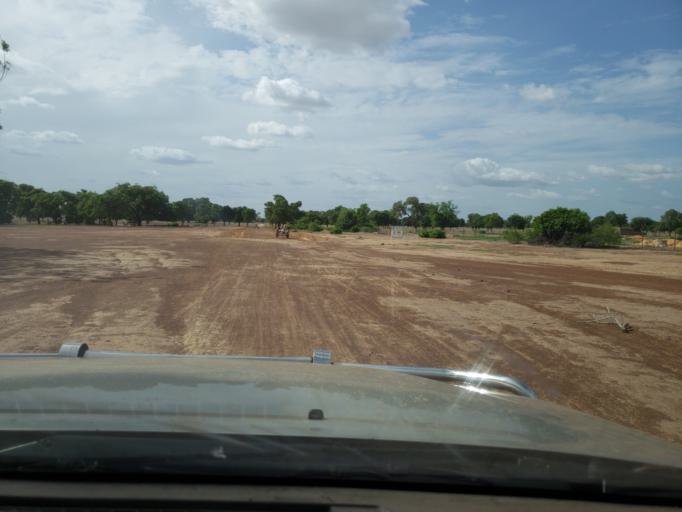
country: ML
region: Segou
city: Bla
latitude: 12.7882
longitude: -5.6047
